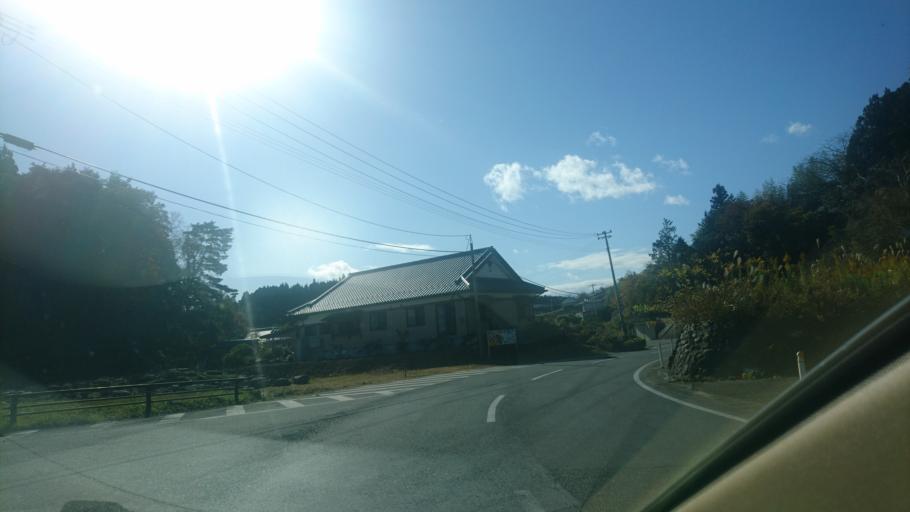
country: JP
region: Iwate
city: Ofunato
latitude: 38.9943
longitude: 141.7264
